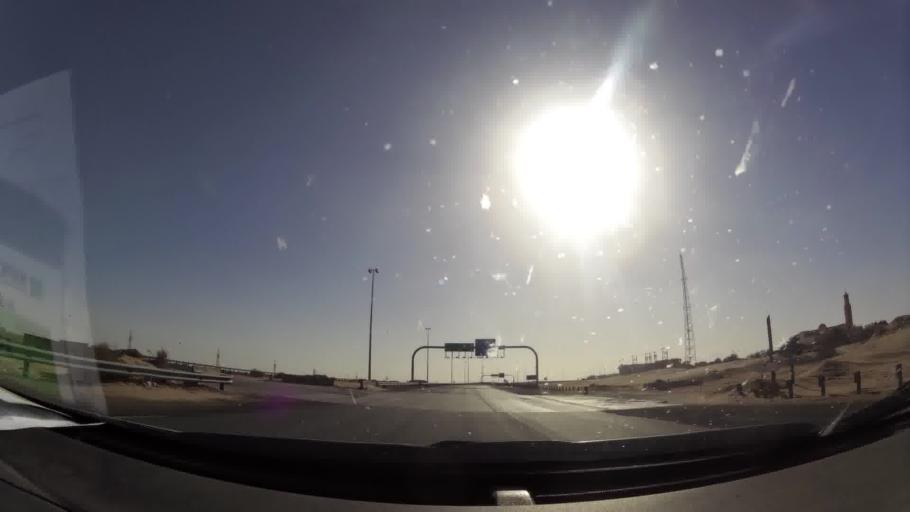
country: KW
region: Al Asimah
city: Kuwait City
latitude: 29.5804
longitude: 47.9046
